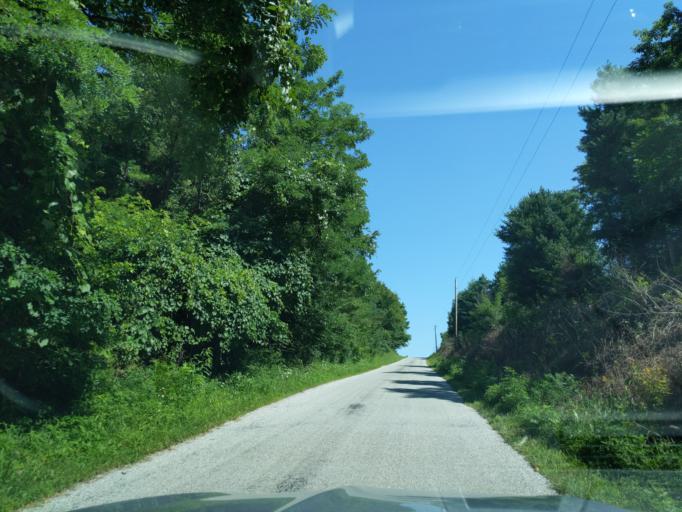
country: US
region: Indiana
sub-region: Ripley County
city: Osgood
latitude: 39.1041
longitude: -85.4322
